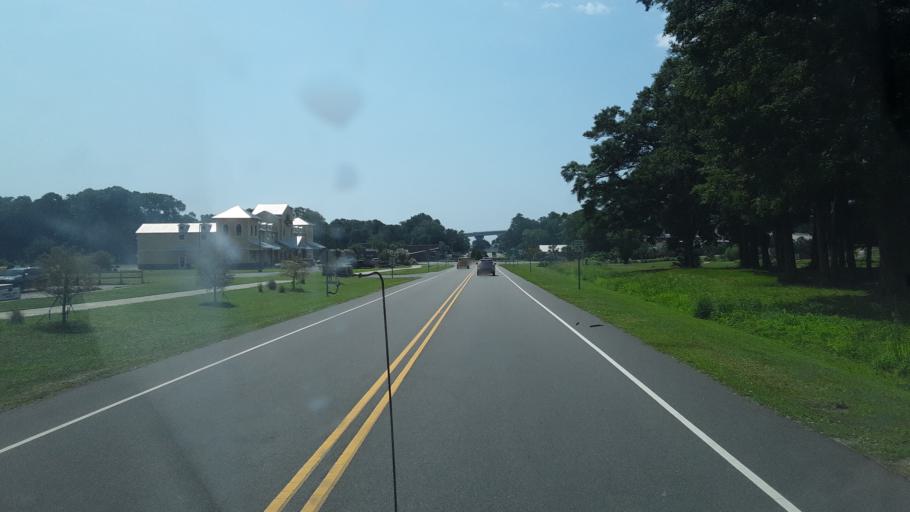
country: US
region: North Carolina
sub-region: Brunswick County
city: Sunset Beach
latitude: 33.8876
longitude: -78.5109
